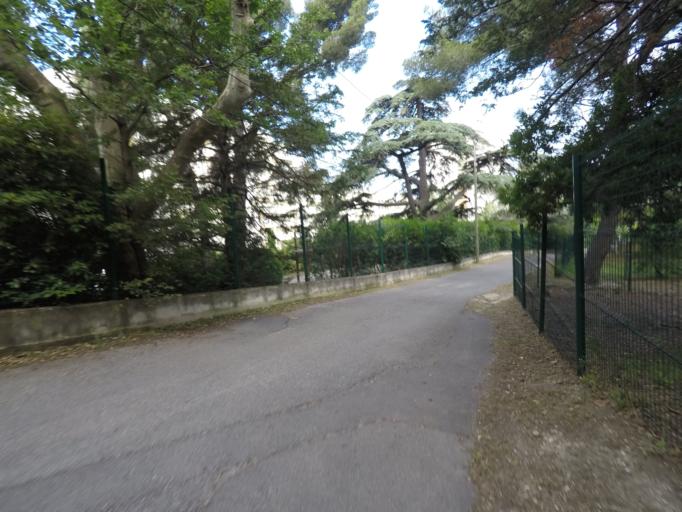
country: FR
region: Provence-Alpes-Cote d'Azur
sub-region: Departement des Bouches-du-Rhone
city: Marseille 09
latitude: 43.2599
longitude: 5.4251
